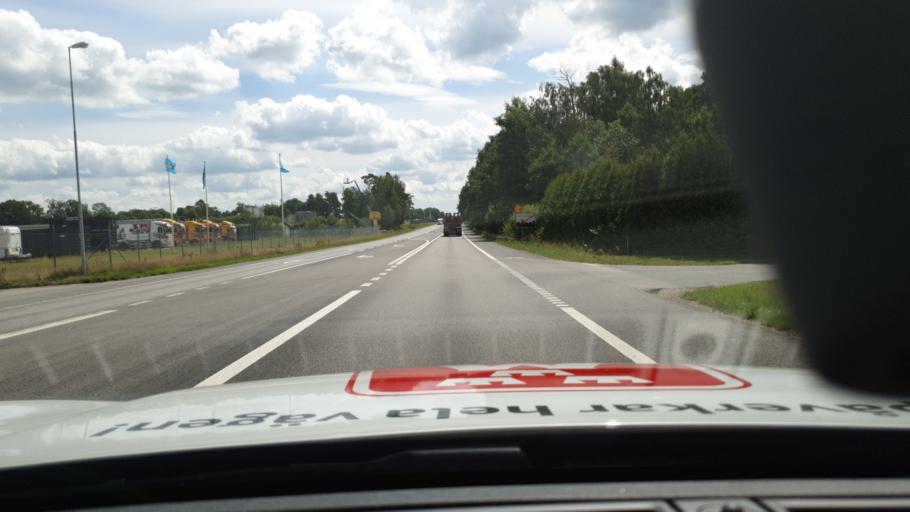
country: SE
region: Skane
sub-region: Hassleholms Kommun
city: Hassleholm
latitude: 56.1454
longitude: 13.7936
